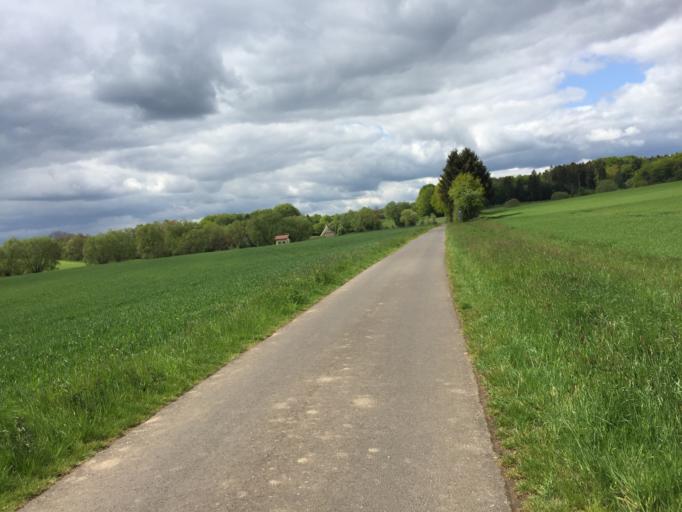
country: DE
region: Hesse
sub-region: Regierungsbezirk Giessen
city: Grunberg
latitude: 50.5717
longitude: 8.9133
